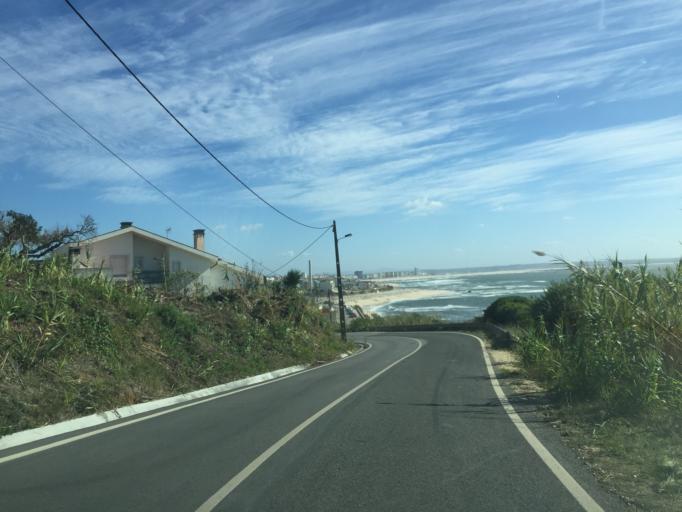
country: PT
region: Coimbra
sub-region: Figueira da Foz
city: Buarcos
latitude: 40.1786
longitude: -8.9017
